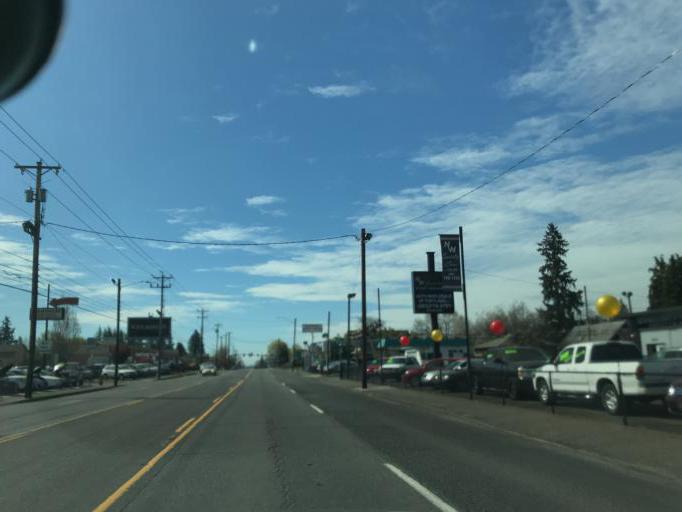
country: US
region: Oregon
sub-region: Multnomah County
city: Lents
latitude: 45.4783
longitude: -122.5791
